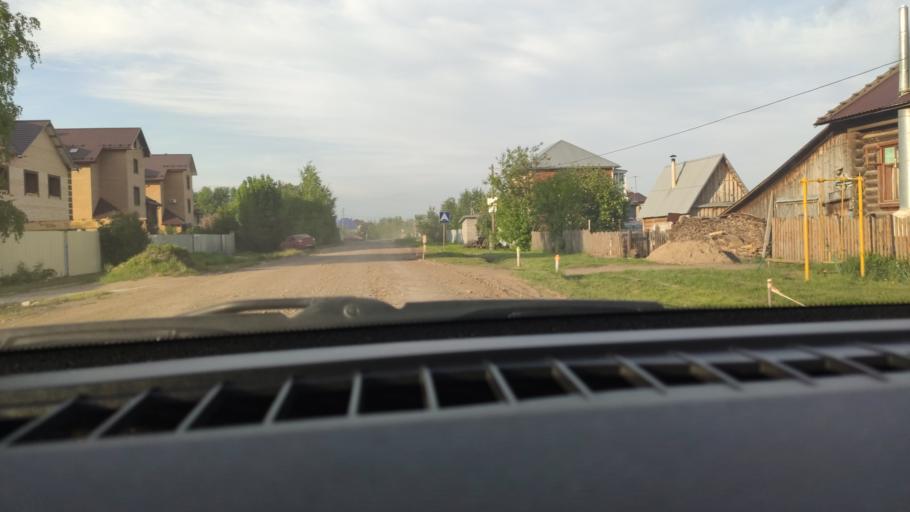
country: RU
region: Perm
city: Kultayevo
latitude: 57.9284
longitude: 56.0131
